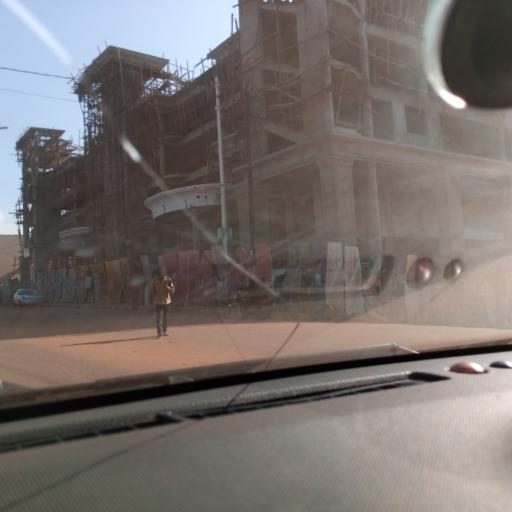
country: UG
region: Central Region
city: Masaka
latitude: -0.3447
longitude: 31.7377
